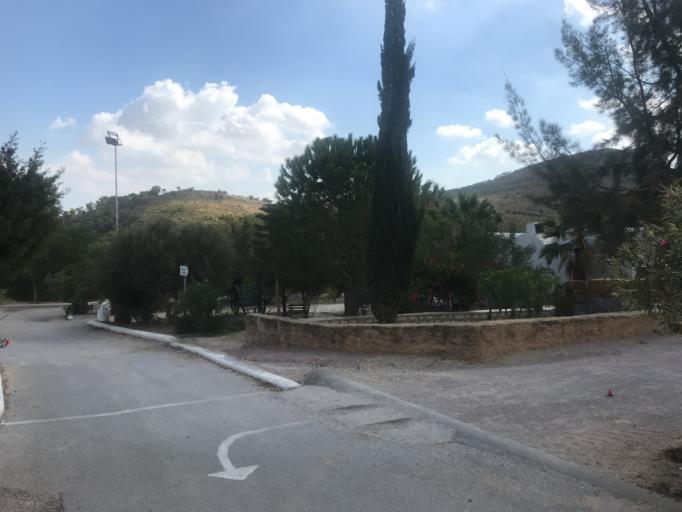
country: TN
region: Ariana
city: Ariana
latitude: 36.8840
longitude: 10.1558
